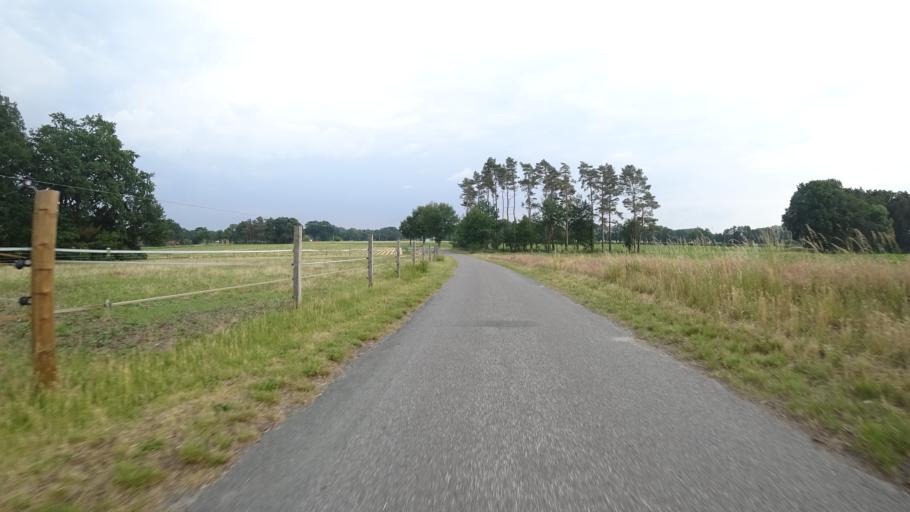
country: DE
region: North Rhine-Westphalia
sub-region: Regierungsbezirk Detmold
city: Guetersloh
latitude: 51.9511
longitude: 8.3700
